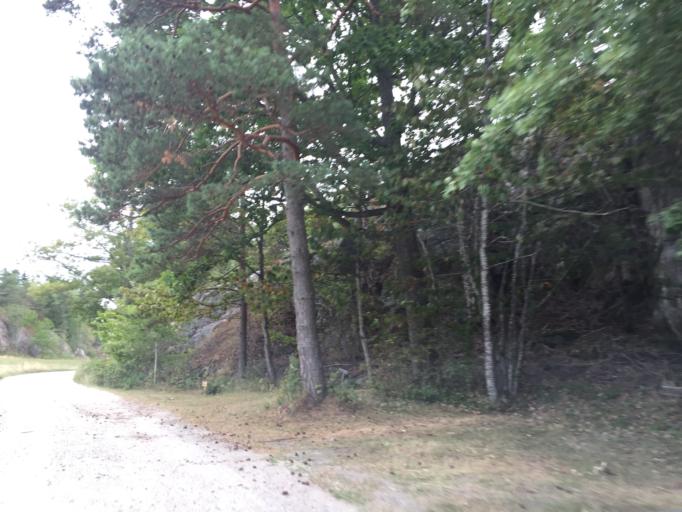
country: NO
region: Ostfold
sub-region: Hvaler
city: Skjaerhalden
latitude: 59.0338
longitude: 11.0562
